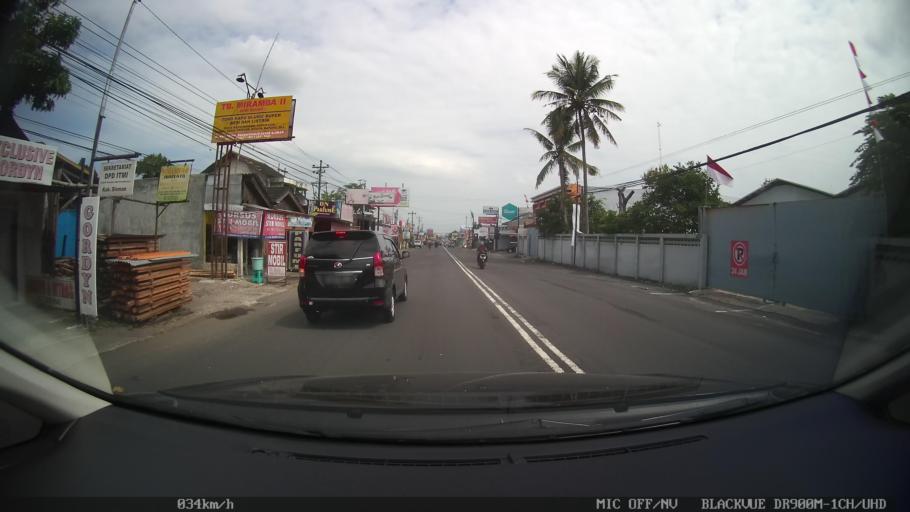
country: ID
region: Daerah Istimewa Yogyakarta
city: Depok
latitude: -7.7542
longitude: 110.4340
